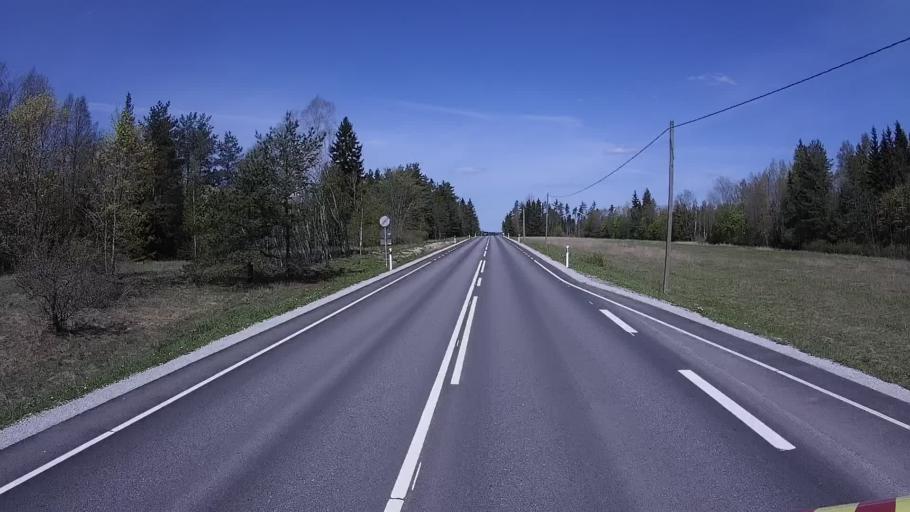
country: EE
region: Harju
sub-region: Paldiski linn
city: Paldiski
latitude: 59.2012
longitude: 24.0969
